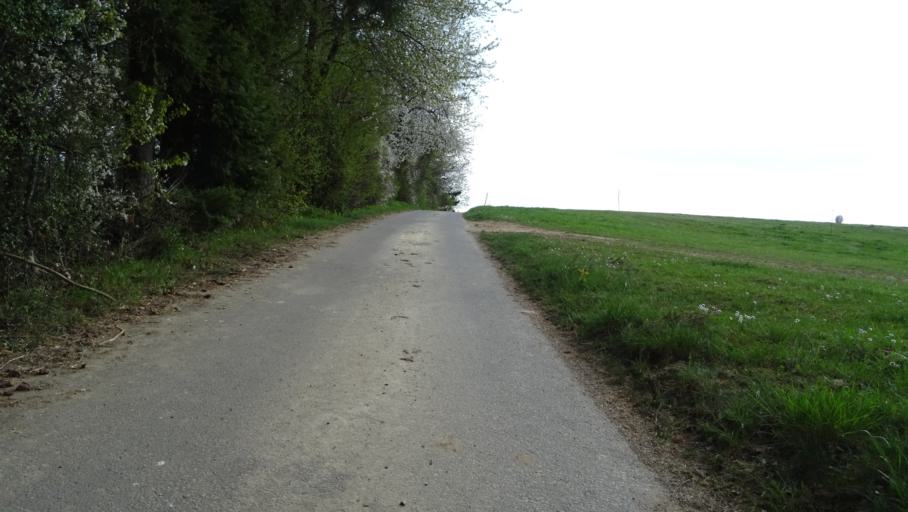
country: DE
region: Baden-Wuerttemberg
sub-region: Karlsruhe Region
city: Billigheim
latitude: 49.3813
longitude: 9.2428
